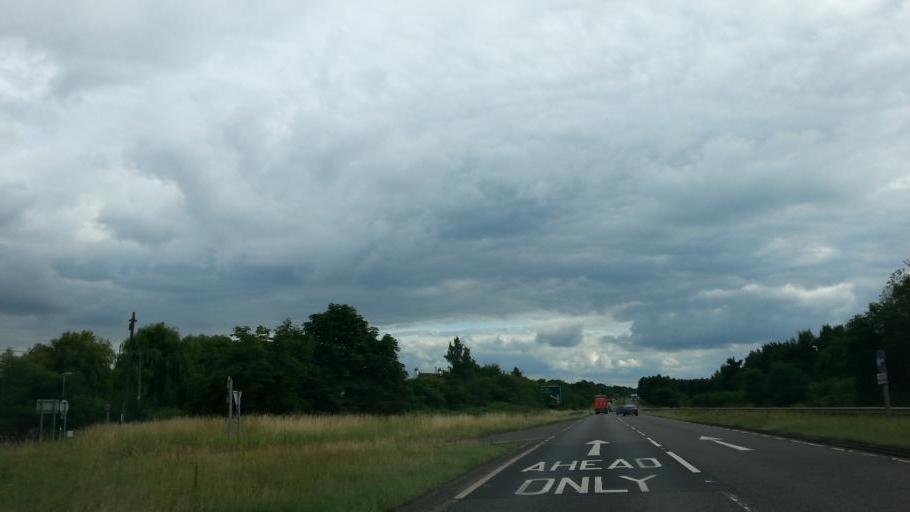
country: GB
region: England
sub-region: Nottinghamshire
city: Babworth
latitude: 53.3256
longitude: -1.0273
